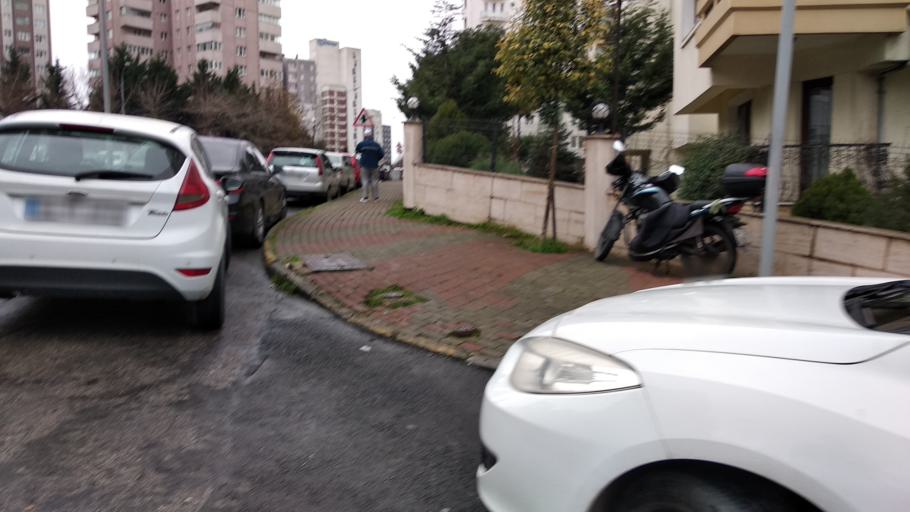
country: TR
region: Istanbul
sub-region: Atasehir
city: Atasehir
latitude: 40.9873
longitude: 29.1239
